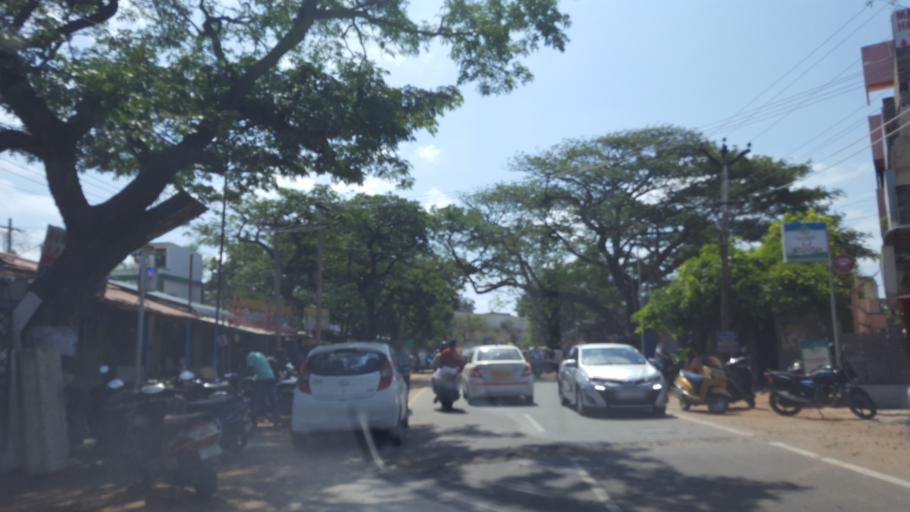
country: IN
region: Tamil Nadu
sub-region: Kancheepuram
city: Mamallapuram
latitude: 12.6223
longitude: 80.1942
